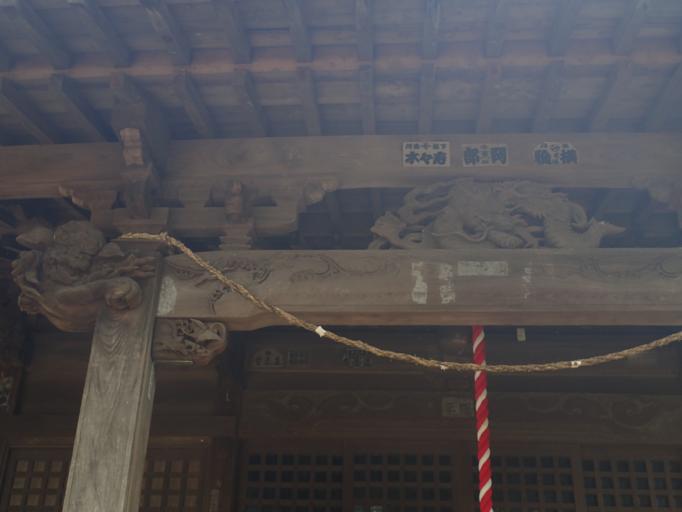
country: JP
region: Kanagawa
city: Zushi
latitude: 35.2976
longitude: 139.6080
